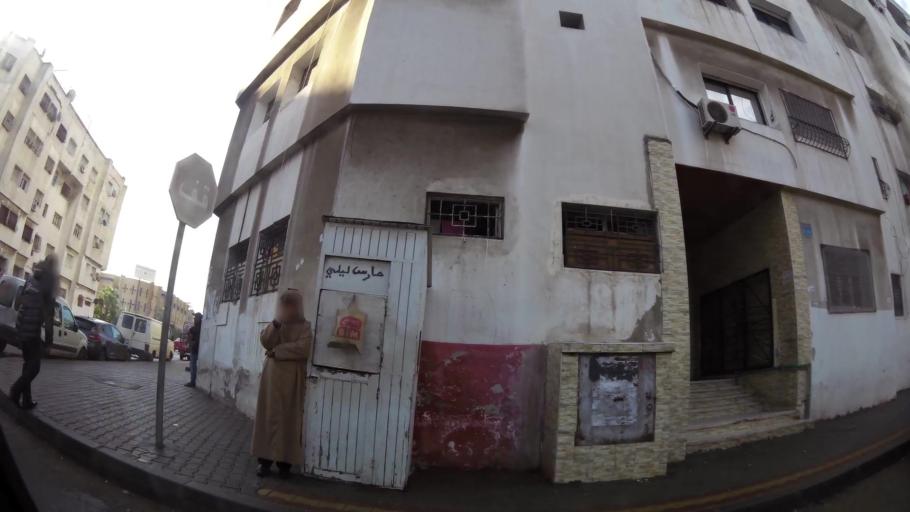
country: MA
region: Grand Casablanca
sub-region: Mediouna
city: Tit Mellil
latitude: 33.5979
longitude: -7.5204
